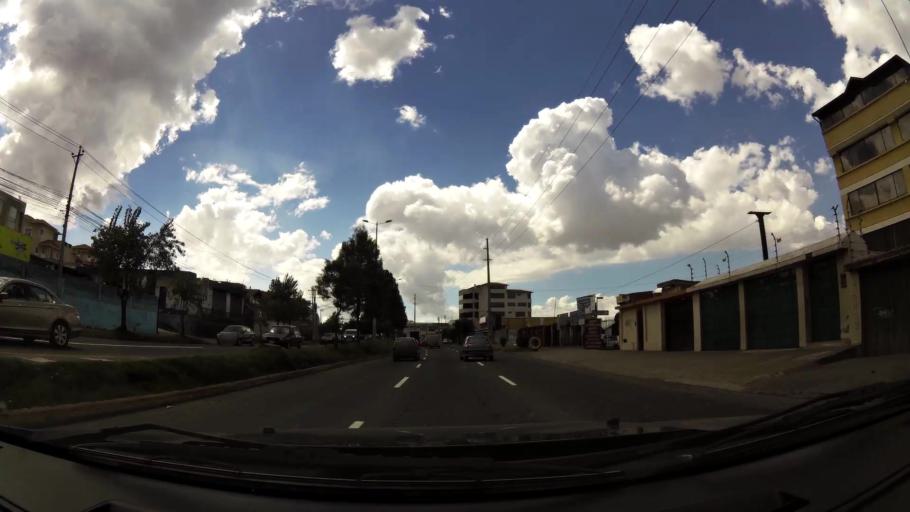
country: EC
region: Pichincha
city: Quito
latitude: -0.1513
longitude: -78.4978
